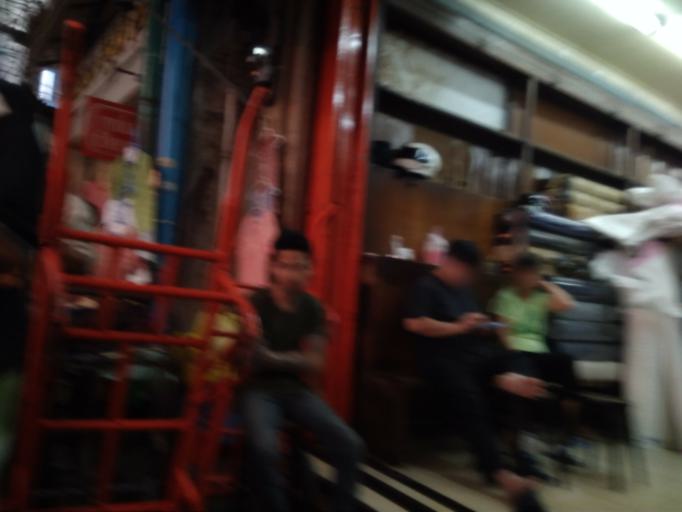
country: TH
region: Bangkok
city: Khlong San
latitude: 13.7417
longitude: 100.5059
